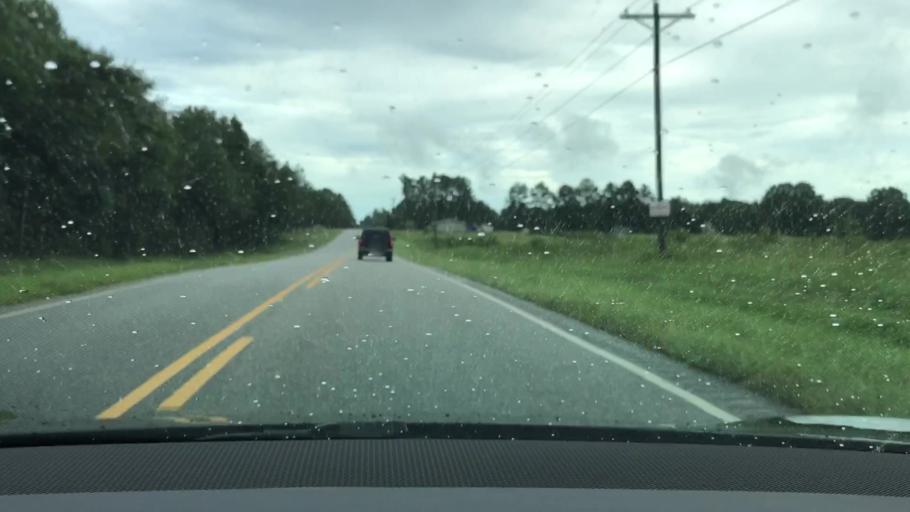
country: US
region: Alabama
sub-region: Geneva County
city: Samson
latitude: 31.0940
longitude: -86.1110
